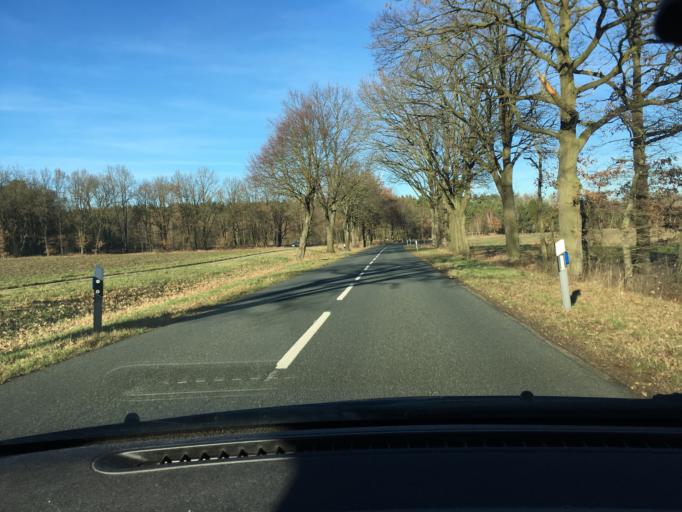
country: DE
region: Lower Saxony
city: Melbeck
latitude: 53.1735
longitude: 10.3814
